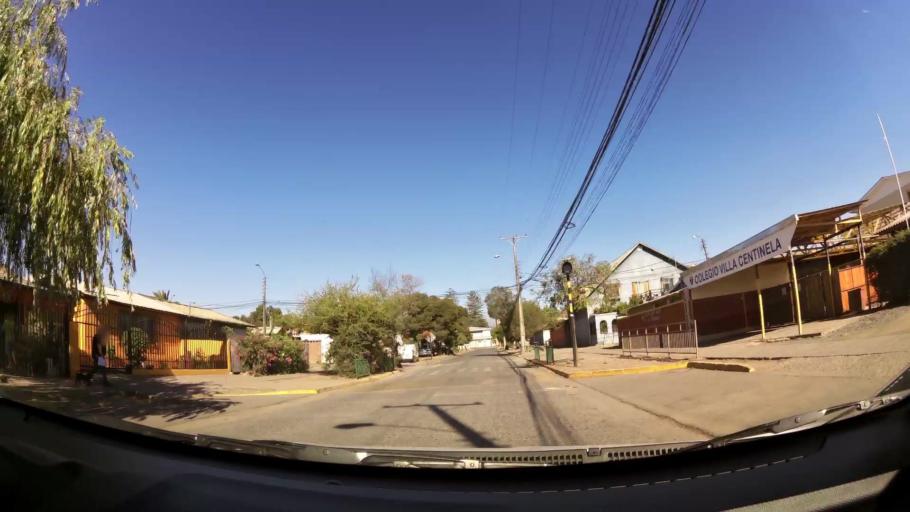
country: CL
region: O'Higgins
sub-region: Provincia de Colchagua
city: Chimbarongo
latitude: -34.5749
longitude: -70.9944
